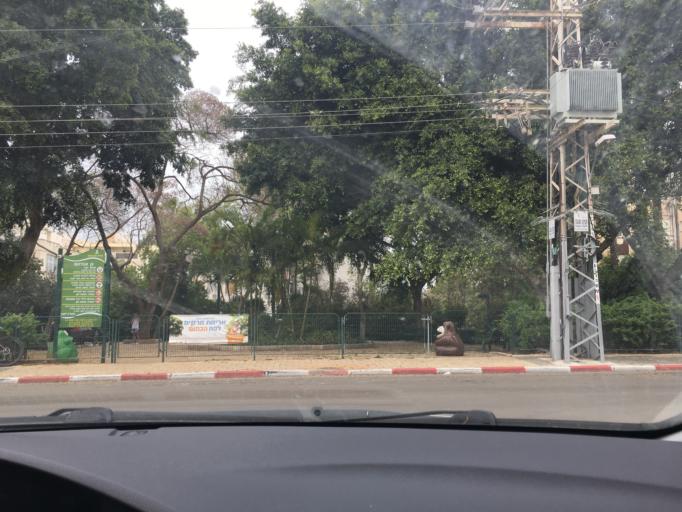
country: IL
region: Tel Aviv
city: Ramat HaSharon
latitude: 32.1430
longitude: 34.8418
